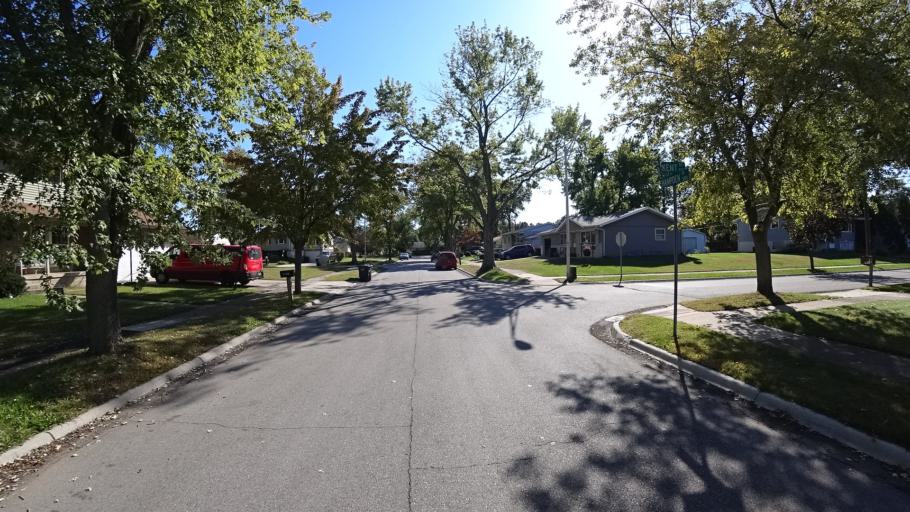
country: US
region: Indiana
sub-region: LaPorte County
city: Michigan City
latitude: 41.6889
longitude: -86.9057
